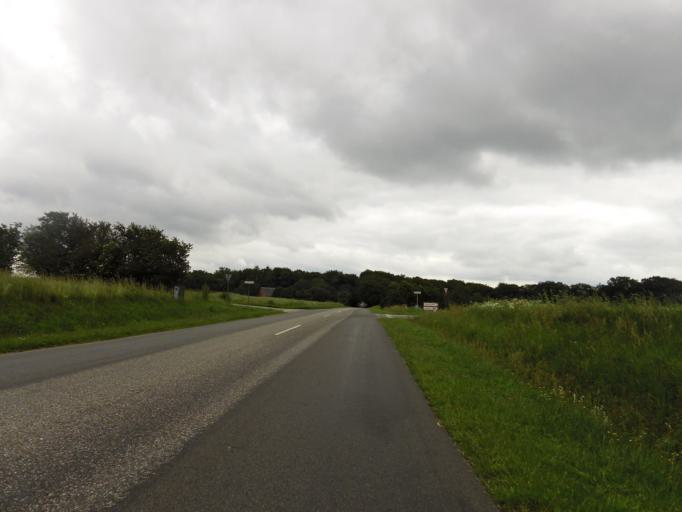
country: DK
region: South Denmark
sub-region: Tonder Kommune
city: Toftlund
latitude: 55.1453
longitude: 9.0476
